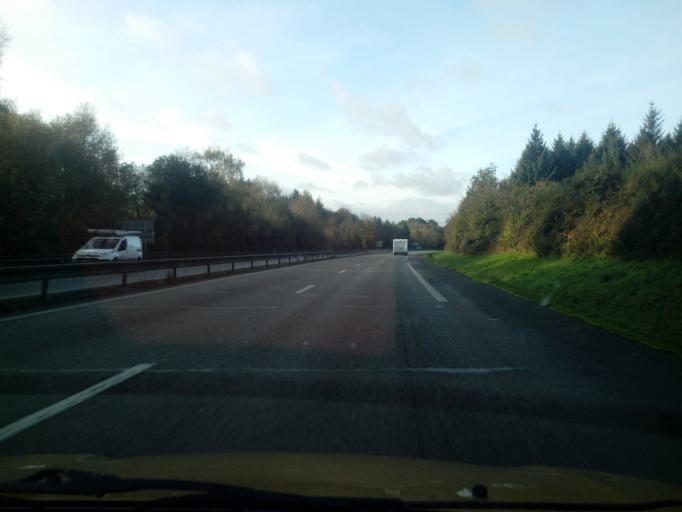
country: FR
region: Brittany
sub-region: Departement du Morbihan
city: Baud
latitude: 47.8872
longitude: -3.0339
